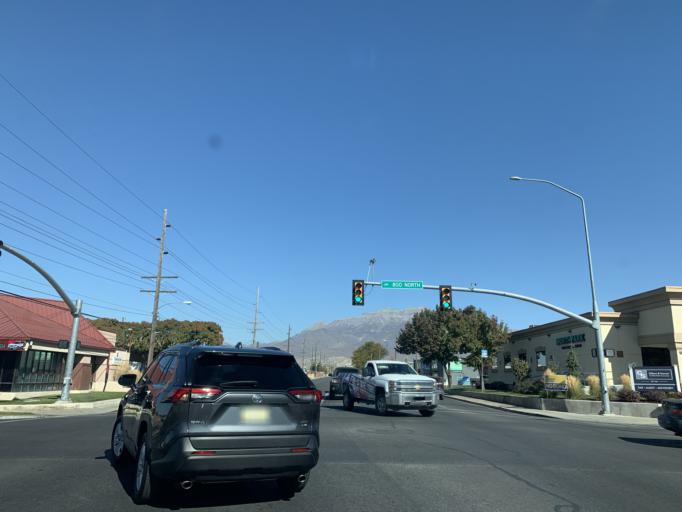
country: US
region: Utah
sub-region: Utah County
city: Provo
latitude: 40.2442
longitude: -111.6621
